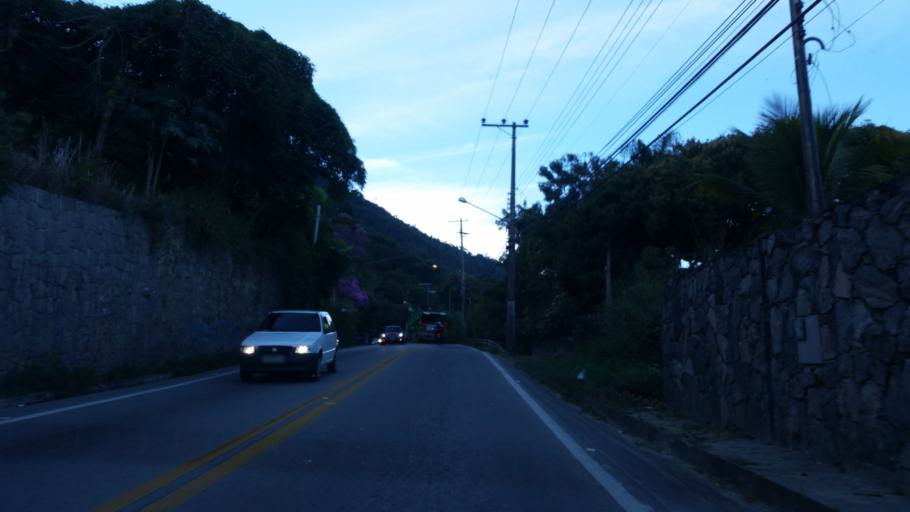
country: BR
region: Sao Paulo
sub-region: Sao Sebastiao
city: Sao Sebastiao
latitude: -23.7464
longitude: -45.4085
